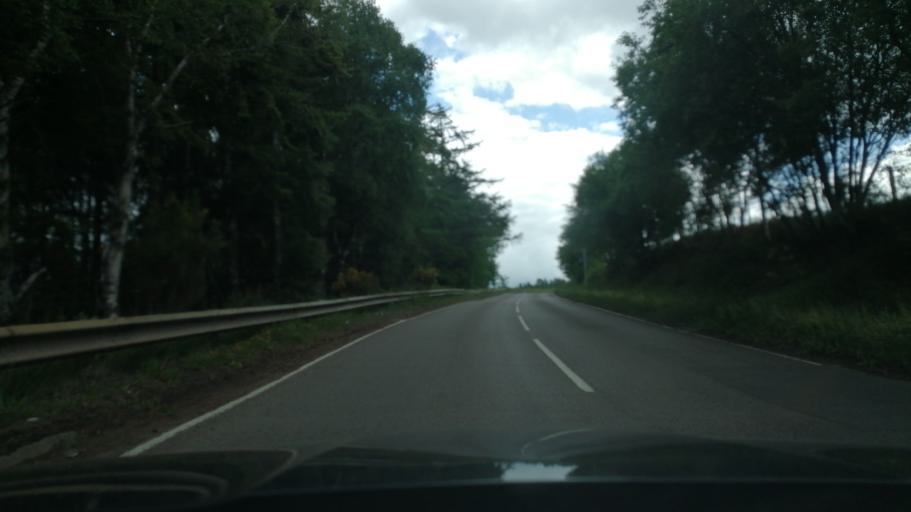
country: GB
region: Scotland
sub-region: Moray
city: Fochabers
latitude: 57.5491
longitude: -3.1308
